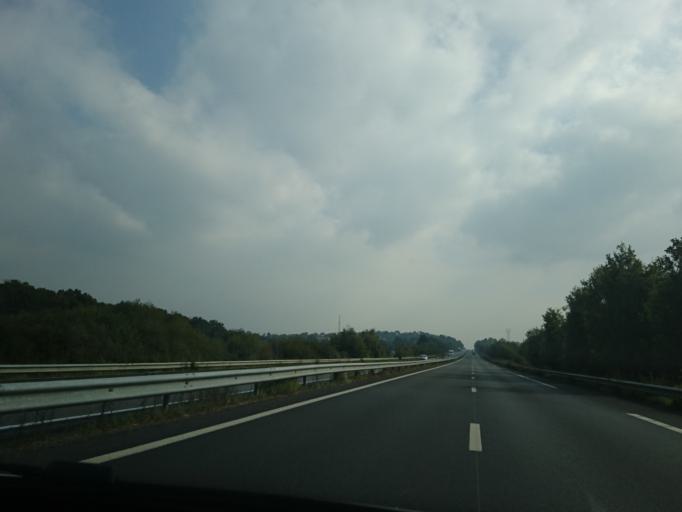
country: FR
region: Pays de la Loire
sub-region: Departement de la Loire-Atlantique
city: Derval
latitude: 47.6857
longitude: -1.6986
